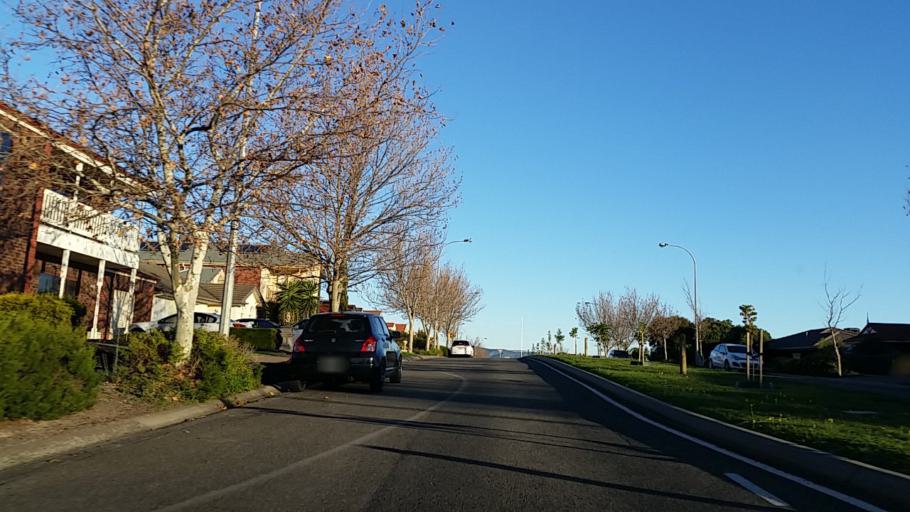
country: AU
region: South Australia
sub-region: Onkaparinga
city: Moana
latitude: -35.2028
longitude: 138.4877
